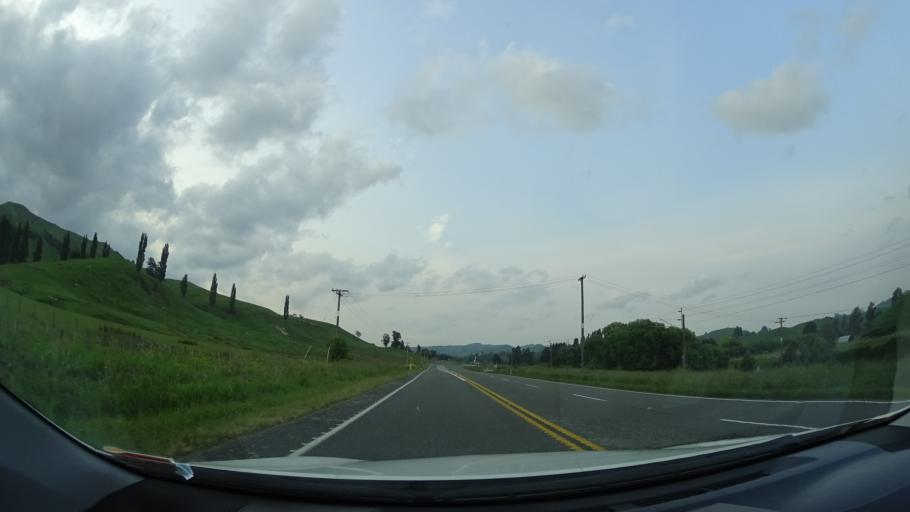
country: NZ
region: Manawatu-Wanganui
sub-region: Ruapehu District
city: Waiouru
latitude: -39.7213
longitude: 175.8409
